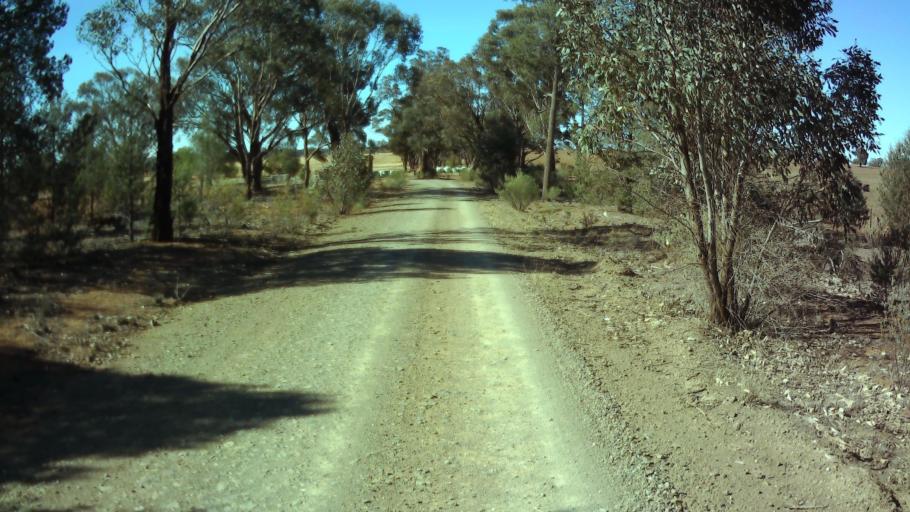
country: AU
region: New South Wales
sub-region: Weddin
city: Grenfell
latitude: -33.7417
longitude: 147.8318
